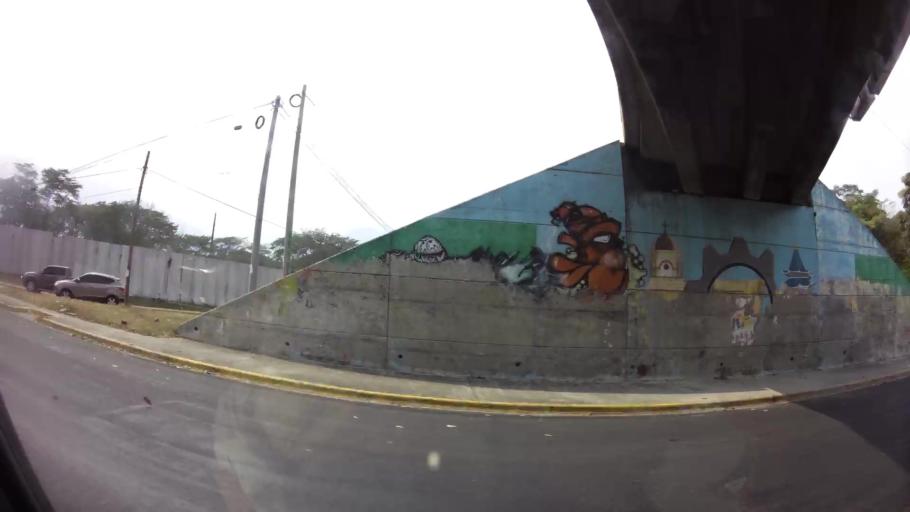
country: HN
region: Cortes
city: San Pedro Sula
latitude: 15.5156
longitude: -88.0320
